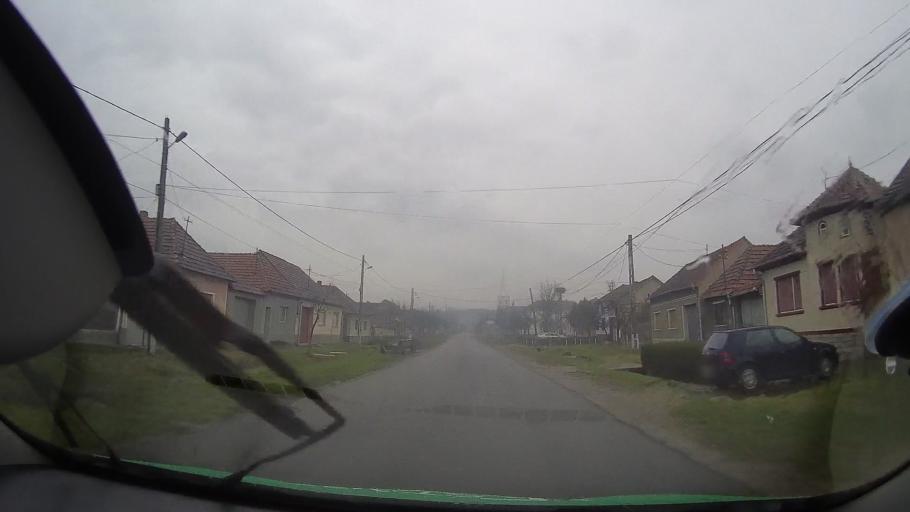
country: RO
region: Bihor
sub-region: Comuna Uileacu de Beius
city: Uileacu de Beius
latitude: 46.6839
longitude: 22.2221
